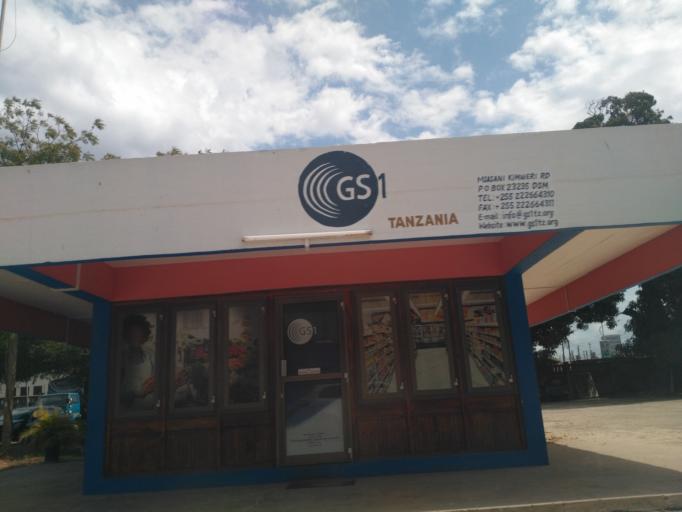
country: TZ
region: Dar es Salaam
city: Magomeni
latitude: -6.7654
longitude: 39.2694
